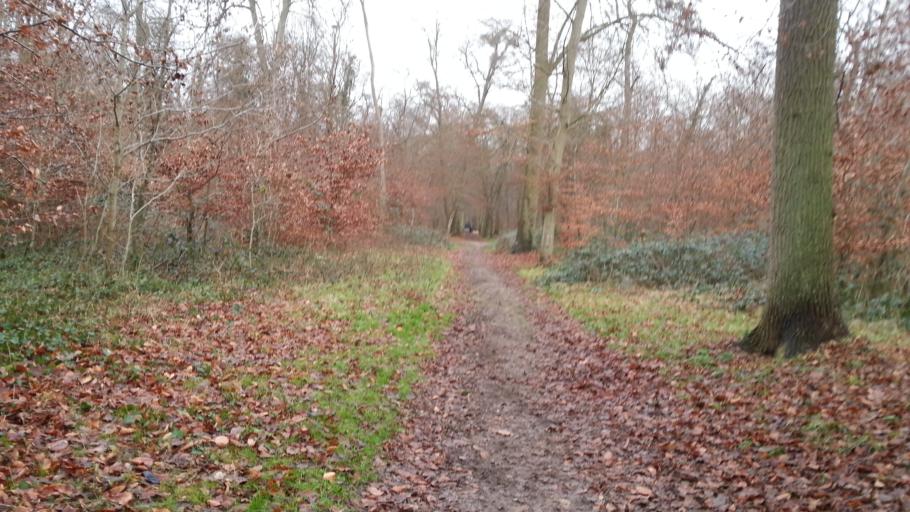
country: FR
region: Picardie
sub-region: Departement de l'Oise
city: Gouvieux
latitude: 49.1850
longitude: 2.3994
